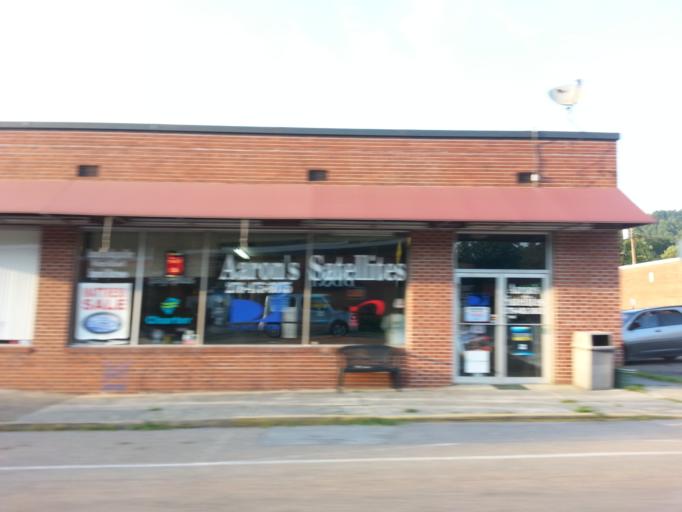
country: US
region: Virginia
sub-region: Washington County
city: Emory
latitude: 36.6354
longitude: -81.7901
